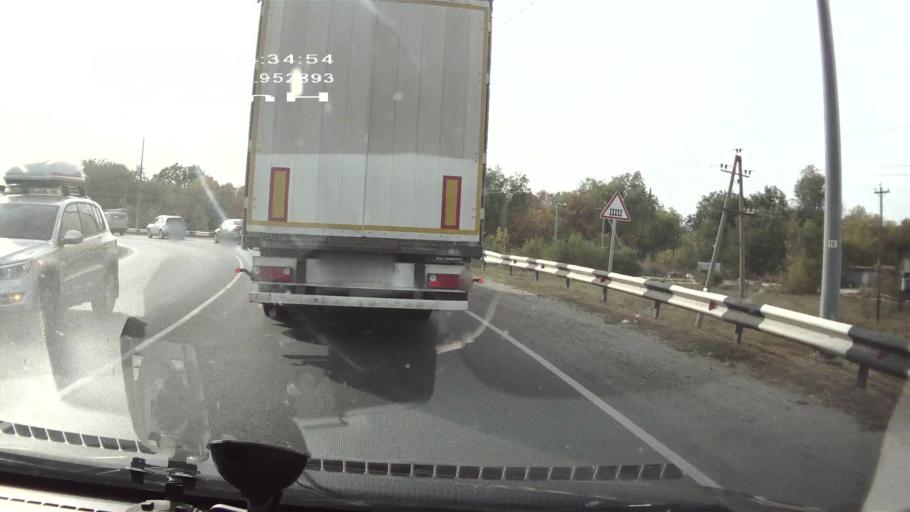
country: RU
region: Saratov
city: Sennoy
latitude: 52.1538
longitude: 46.9536
